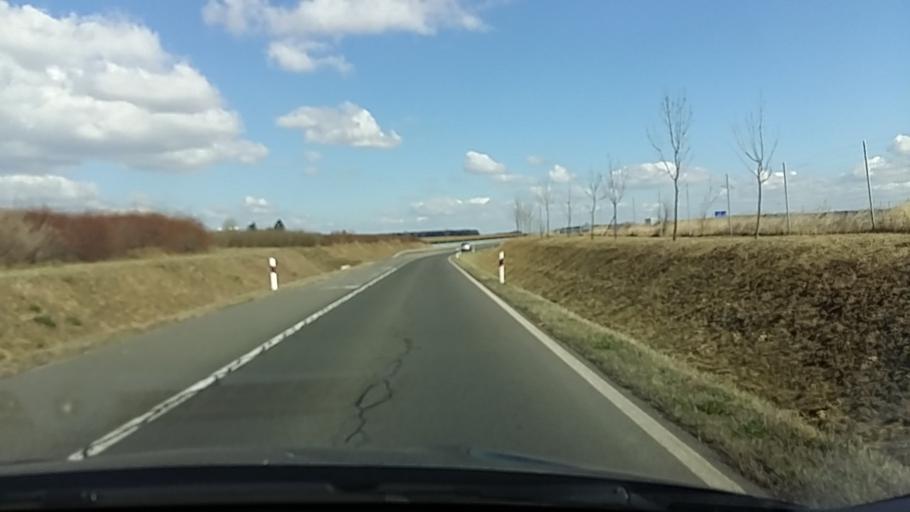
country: HU
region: Baranya
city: Kozarmisleny
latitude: 46.0184
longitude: 18.2896
